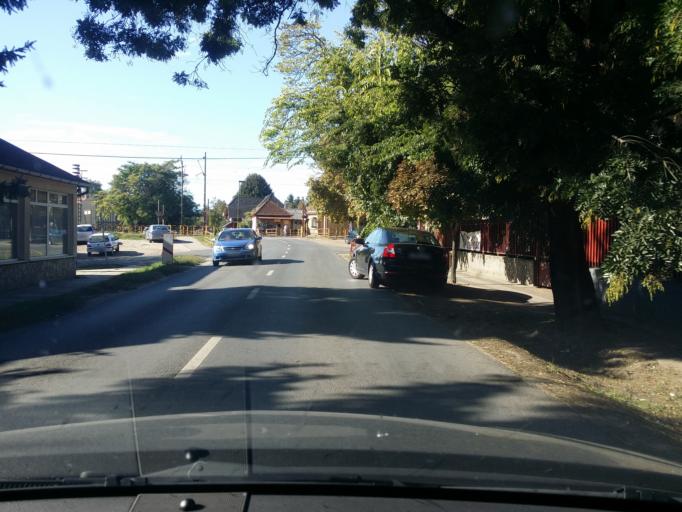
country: HU
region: Pest
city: God
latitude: 47.7049
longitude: 19.1440
